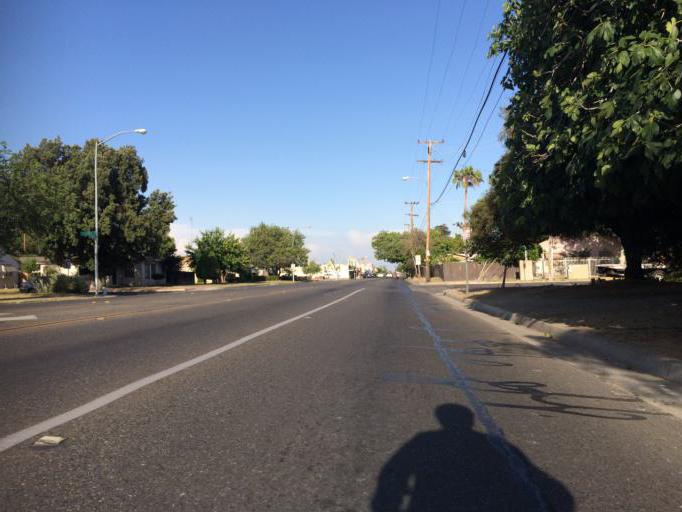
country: US
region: California
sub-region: Fresno County
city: Fresno
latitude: 36.7431
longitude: -119.7569
